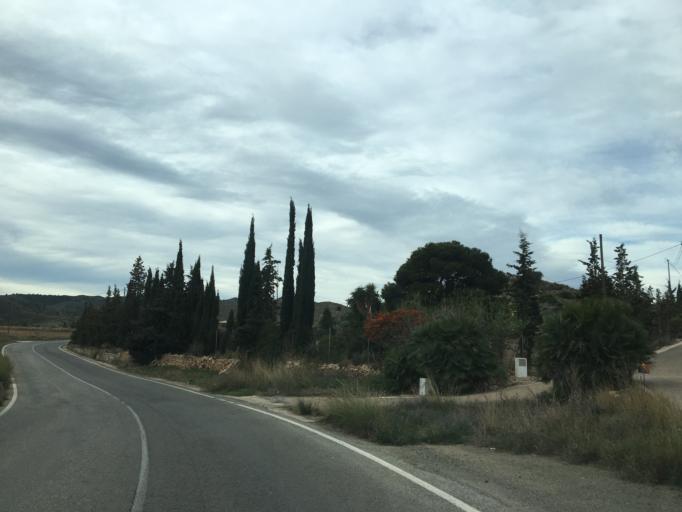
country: ES
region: Murcia
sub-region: Murcia
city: Fuente-Alamo de Murcia
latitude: 37.6145
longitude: -1.0974
